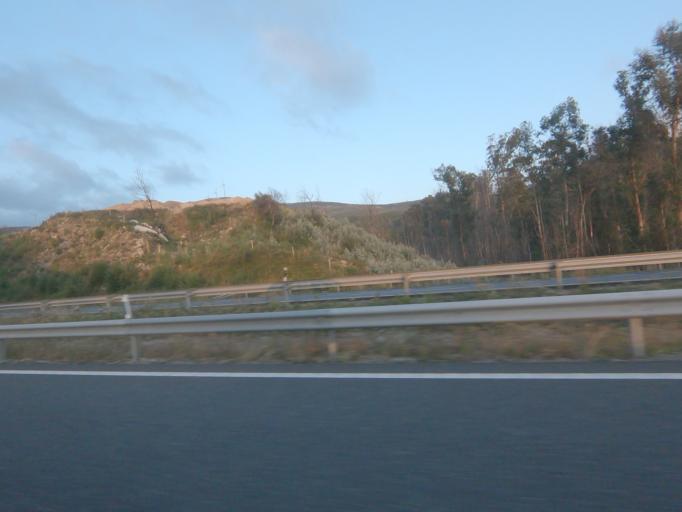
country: ES
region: Galicia
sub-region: Provincia de Pontevedra
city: Covelo
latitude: 42.1604
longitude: -8.3980
